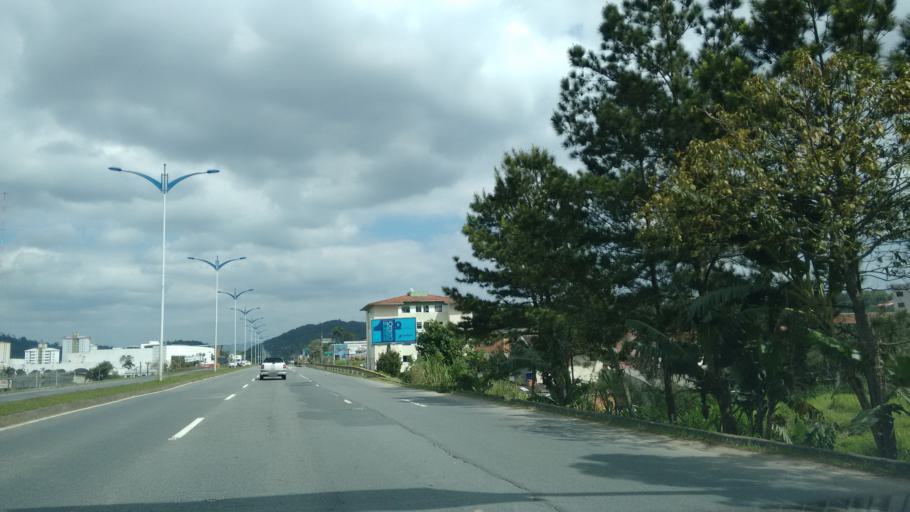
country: BR
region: Santa Catarina
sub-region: Blumenau
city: Blumenau
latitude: -26.8807
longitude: -49.0695
